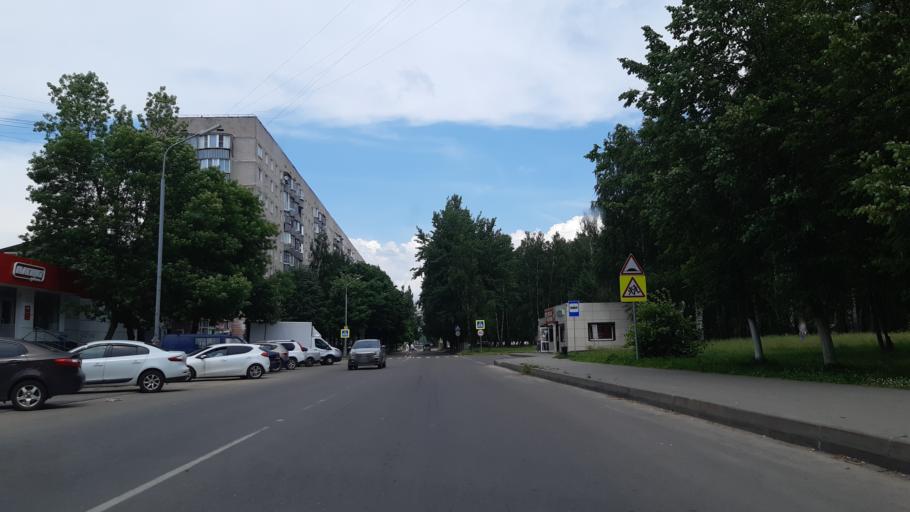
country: RU
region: Smolensk
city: Desnogorsk
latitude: 54.1542
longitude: 33.2887
